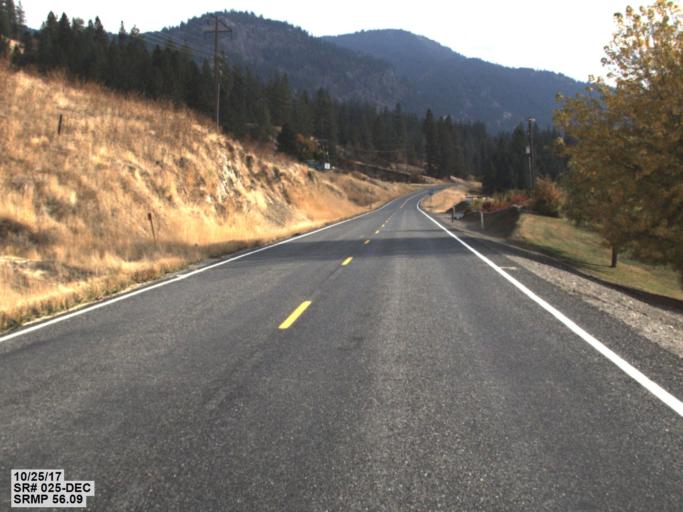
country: US
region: Washington
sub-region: Stevens County
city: Kettle Falls
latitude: 48.2851
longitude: -118.1384
